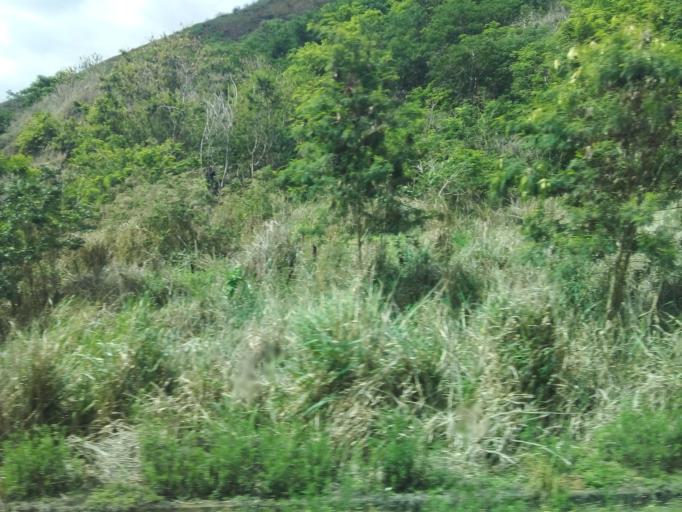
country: BR
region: Minas Gerais
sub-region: Governador Valadares
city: Governador Valadares
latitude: -18.9242
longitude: -42.0235
